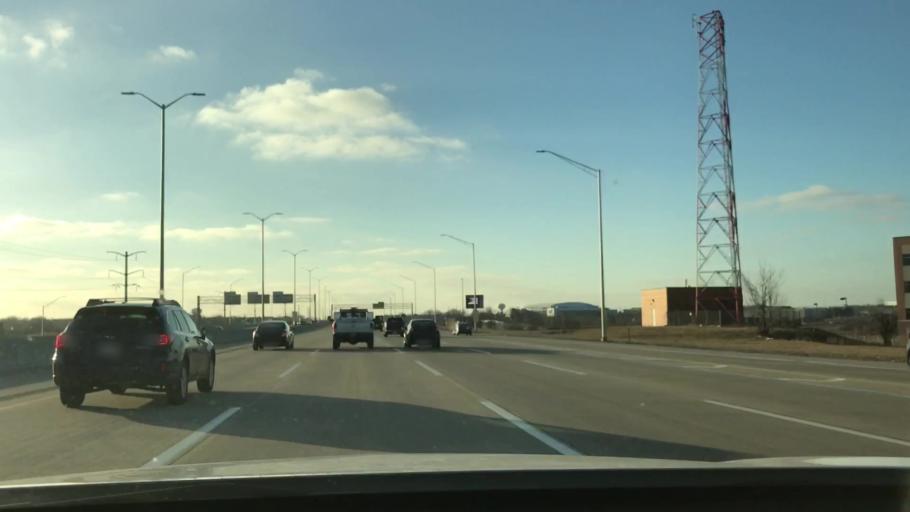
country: US
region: Illinois
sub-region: Cook County
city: Streamwood
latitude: 42.0670
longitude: -88.1974
